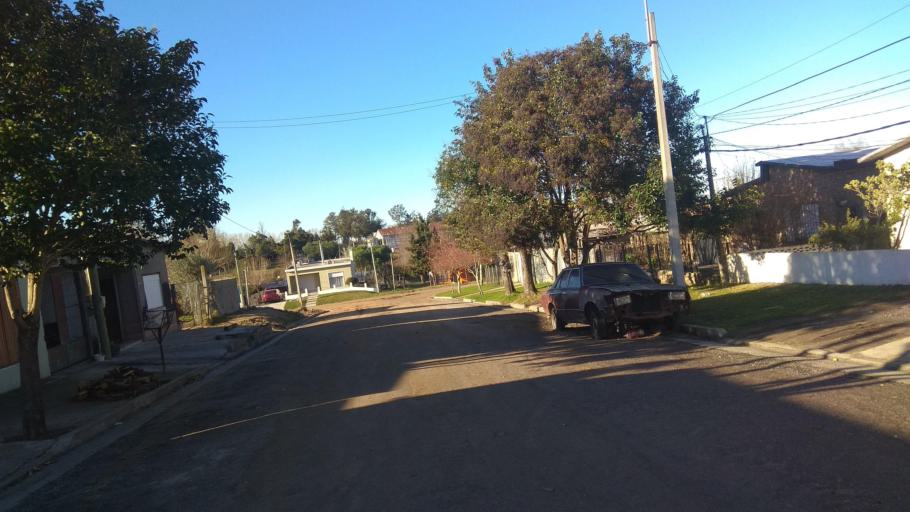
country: UY
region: Florida
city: Florida
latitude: -34.0979
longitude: -56.2374
